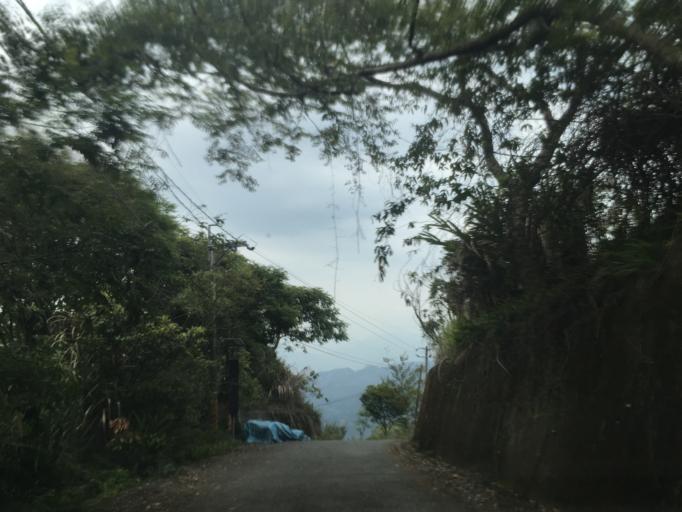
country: TW
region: Taiwan
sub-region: Nantou
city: Puli
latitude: 23.9621
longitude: 120.8449
